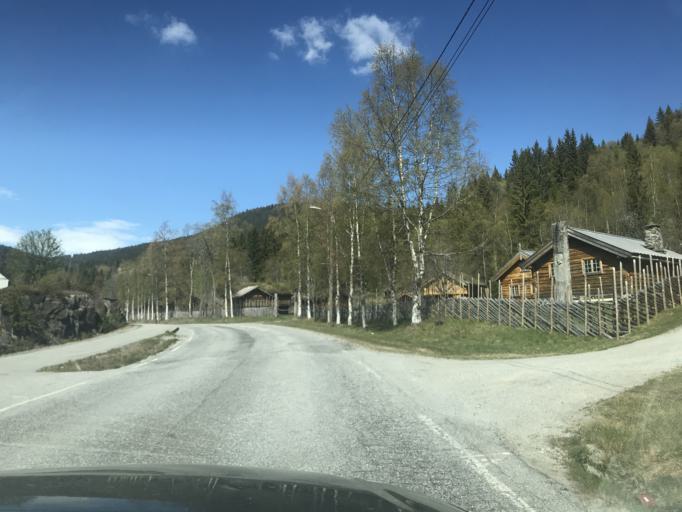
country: NO
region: Telemark
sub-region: Hjartdal
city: Sauland
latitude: 59.7533
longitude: 8.7965
